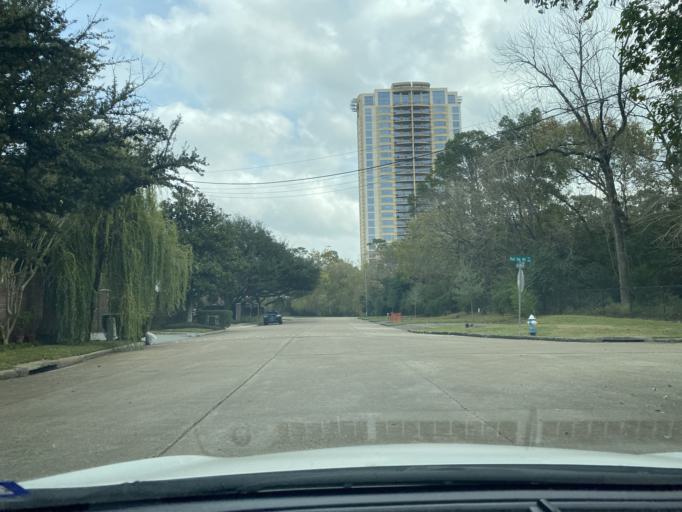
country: US
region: Texas
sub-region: Harris County
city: Hunters Creek Village
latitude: 29.7589
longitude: -95.4602
